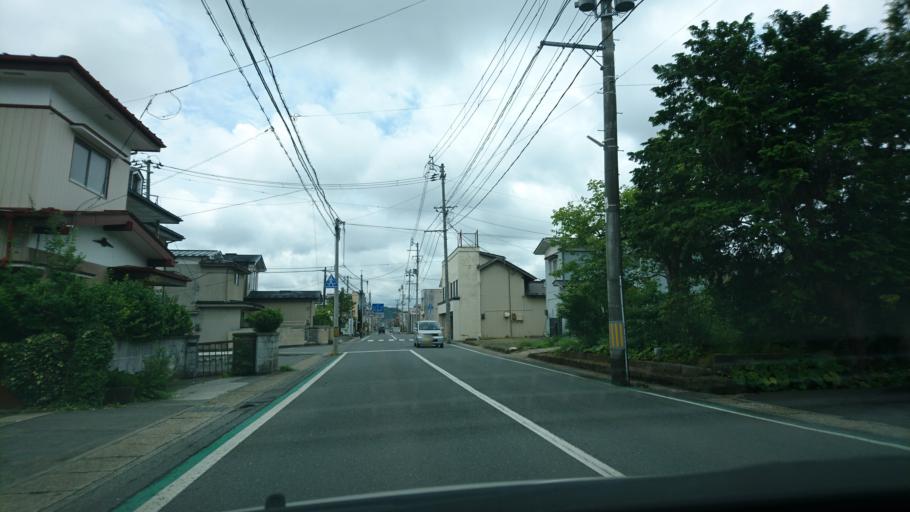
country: JP
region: Iwate
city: Ichinoseki
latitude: 38.9469
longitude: 141.1299
